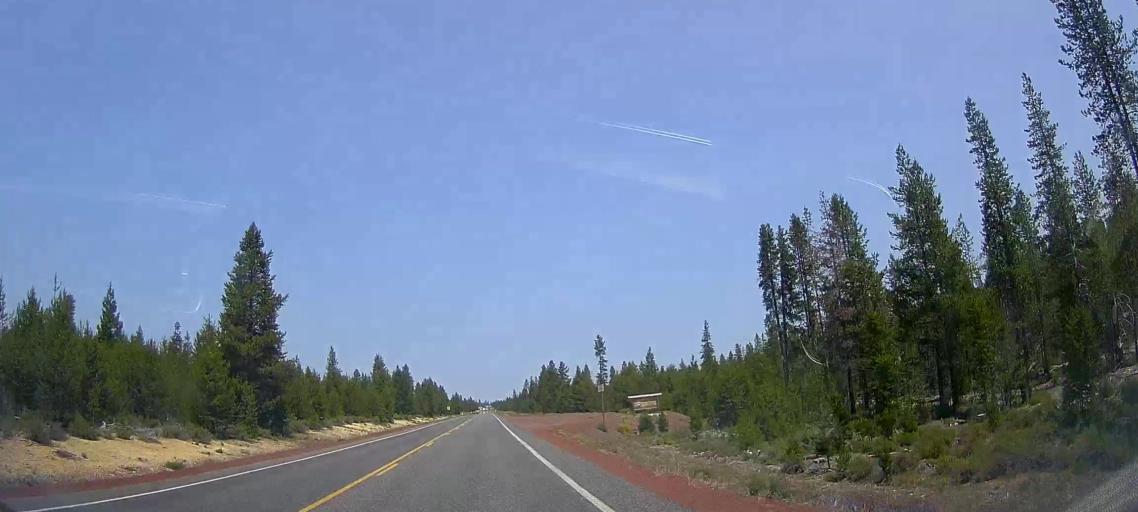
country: US
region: Oregon
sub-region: Deschutes County
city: La Pine
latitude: 43.3857
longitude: -121.7296
